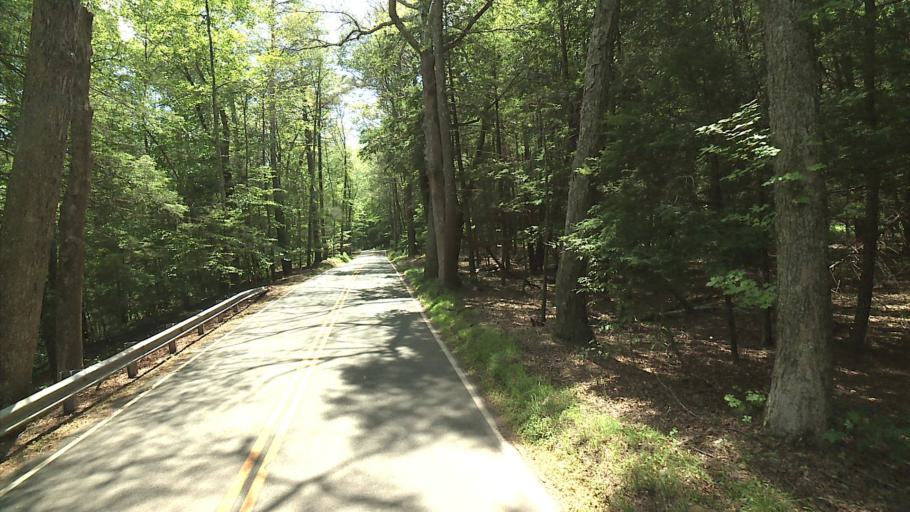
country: US
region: Connecticut
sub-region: New London County
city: Colchester
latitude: 41.4663
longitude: -72.3379
